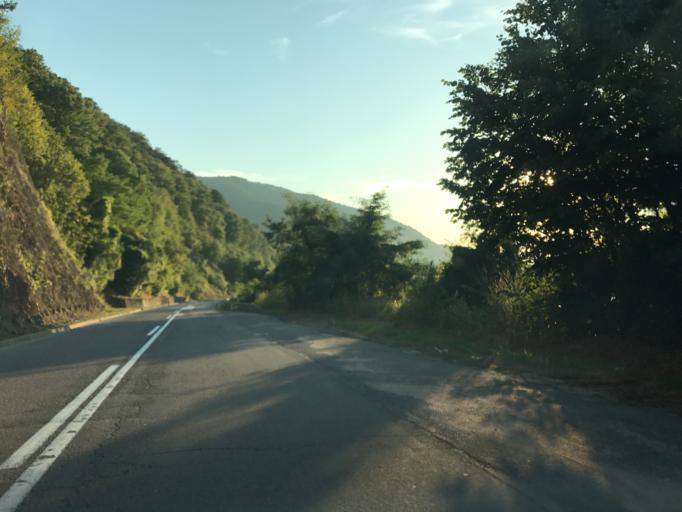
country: RO
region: Caras-Severin
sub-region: Comuna Berzasca
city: Berzasca
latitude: 44.6301
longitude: 21.9699
